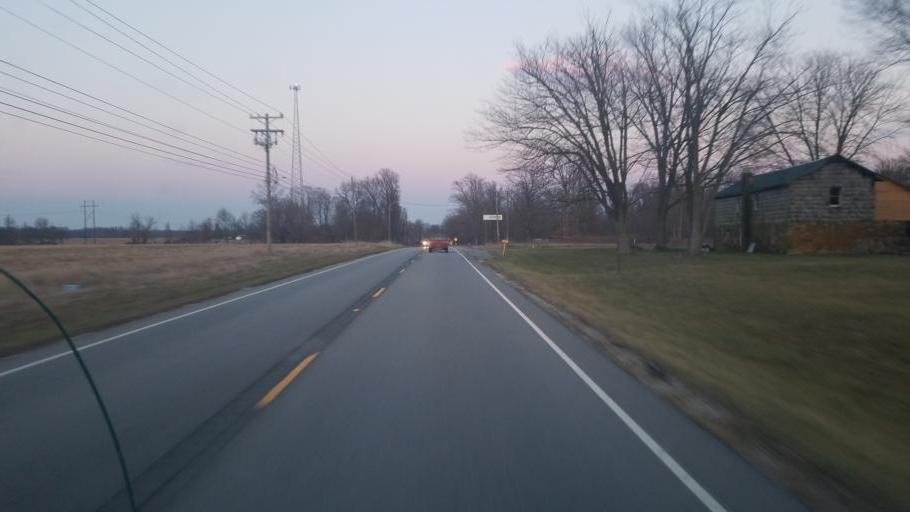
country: US
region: Indiana
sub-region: Lawrence County
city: Bedford
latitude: 38.8816
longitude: -86.2708
